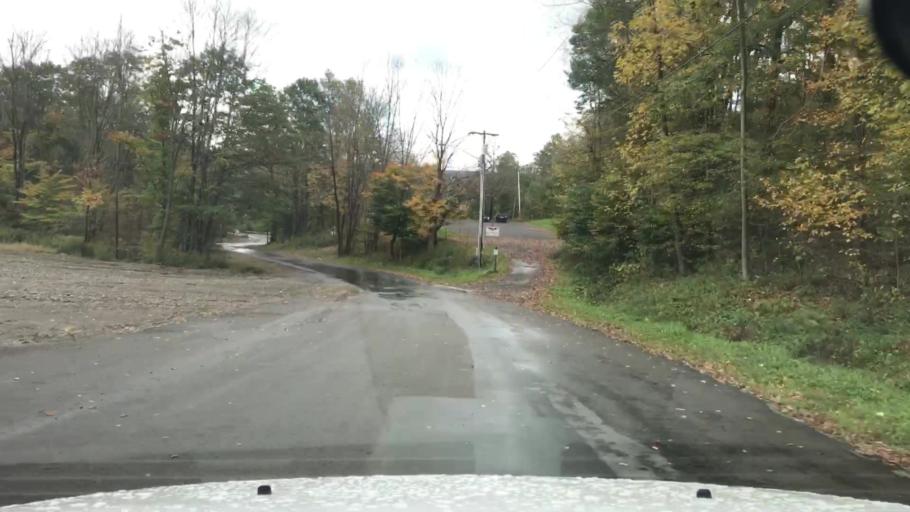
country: US
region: New York
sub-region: Cattaraugus County
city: Salamanca
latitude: 42.2627
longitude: -78.6807
